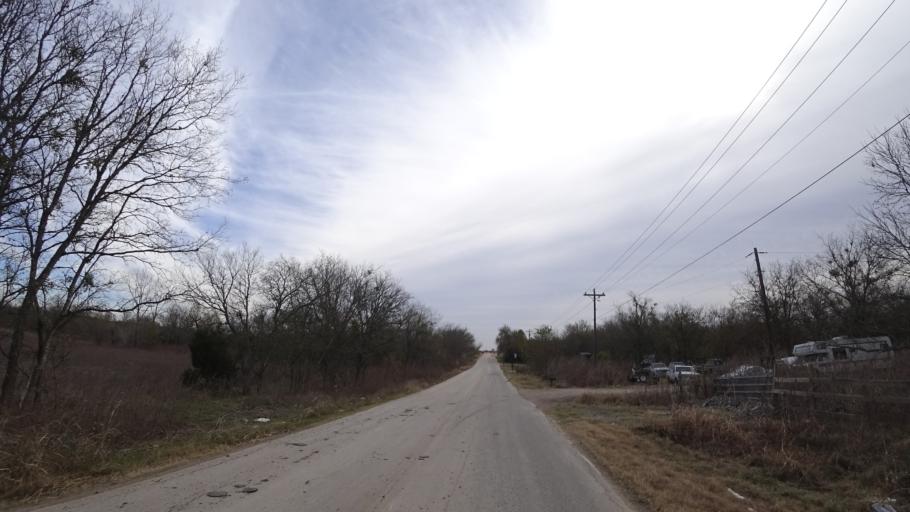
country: US
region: Texas
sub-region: Travis County
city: Onion Creek
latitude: 30.1558
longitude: -97.7223
